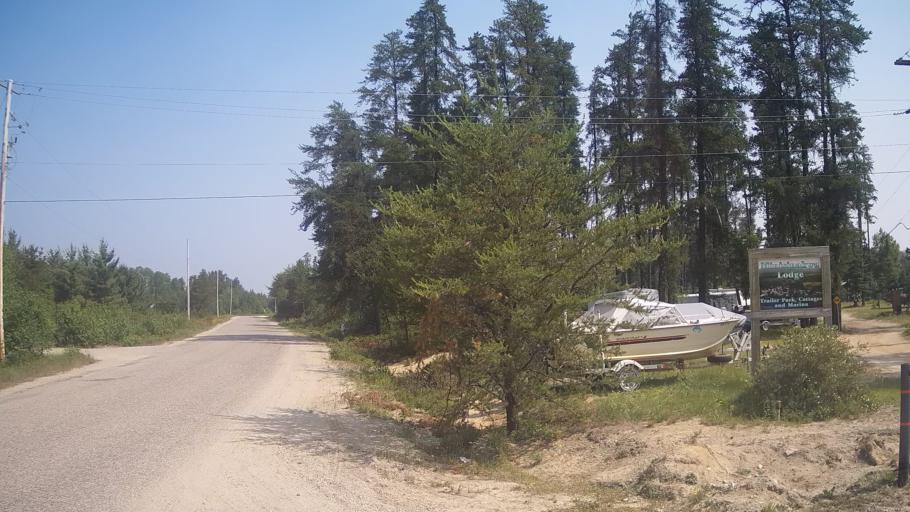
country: CA
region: Ontario
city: Timmins
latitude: 47.6828
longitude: -81.7139
